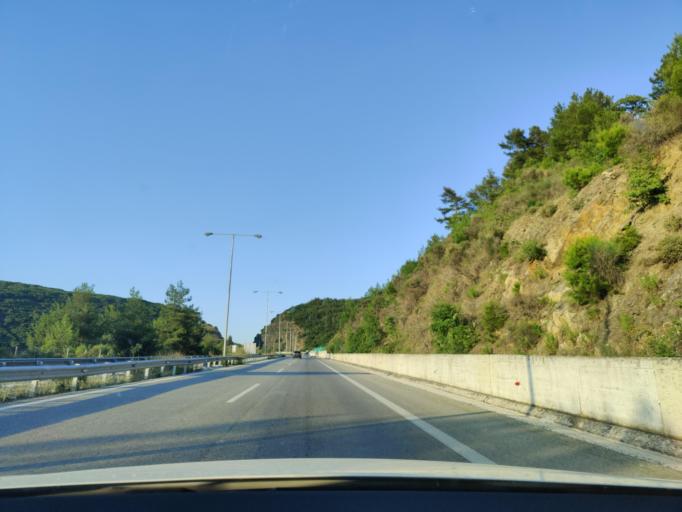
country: GR
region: East Macedonia and Thrace
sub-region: Nomos Kavalas
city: Amygdaleonas
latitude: 40.9497
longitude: 24.3768
